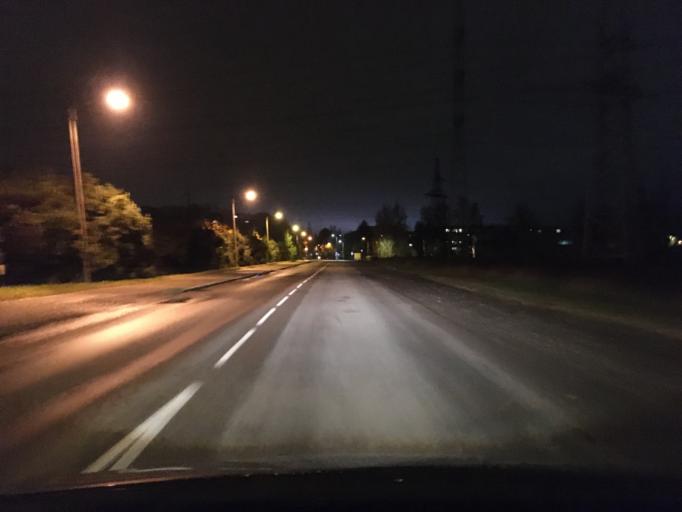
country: EE
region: Tartu
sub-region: Tartu linn
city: Tartu
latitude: 58.3804
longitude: 26.6843
